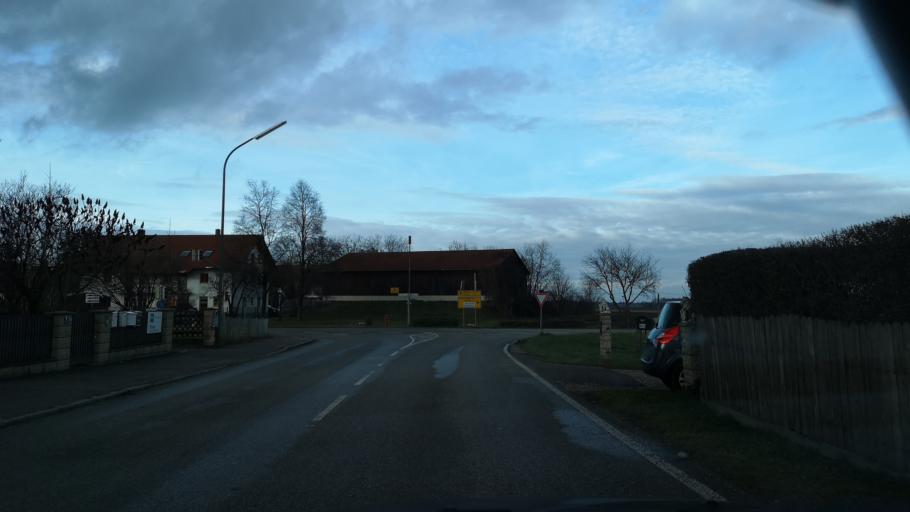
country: DE
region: Bavaria
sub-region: Upper Bavaria
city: Pliening
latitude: 48.1953
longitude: 11.8036
